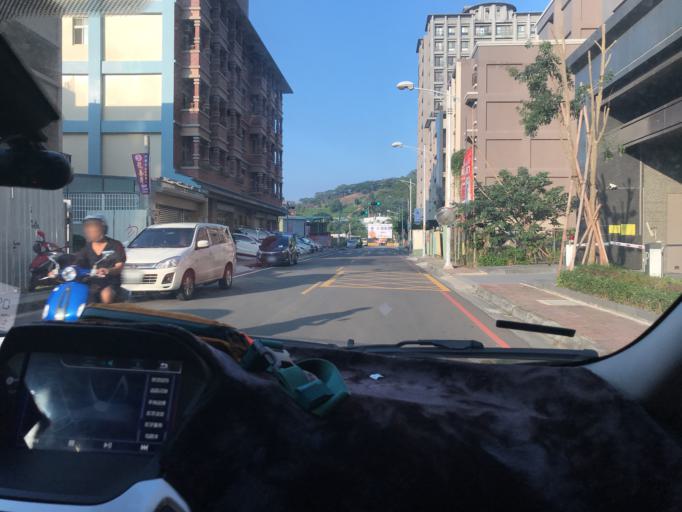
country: TW
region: Taiwan
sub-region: Hsinchu
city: Zhubei
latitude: 24.8242
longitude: 121.0340
